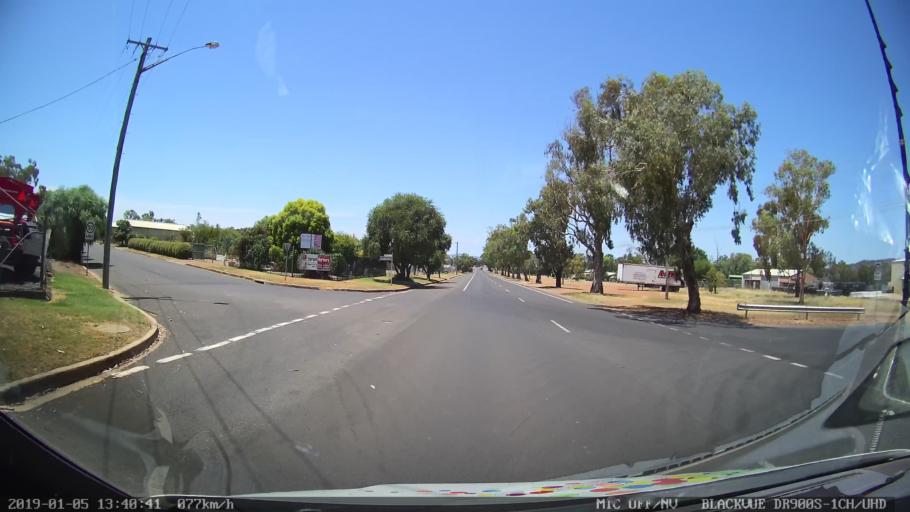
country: AU
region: New South Wales
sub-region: Gunnedah
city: Gunnedah
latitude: -30.9809
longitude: 150.2322
